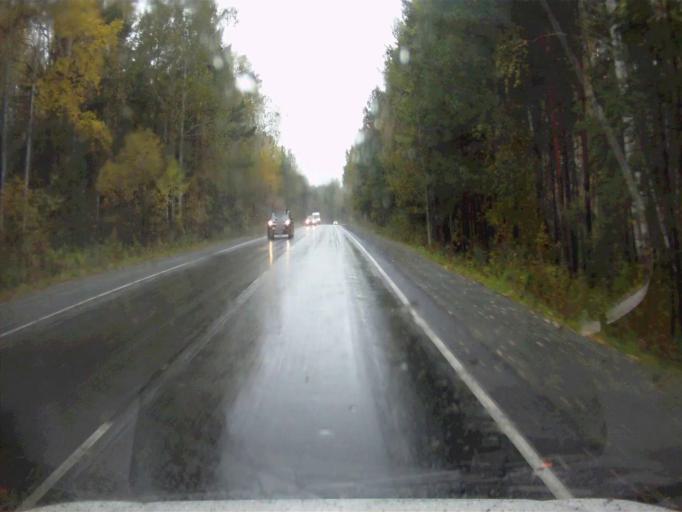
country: RU
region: Chelyabinsk
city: Tayginka
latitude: 55.5943
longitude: 60.6223
